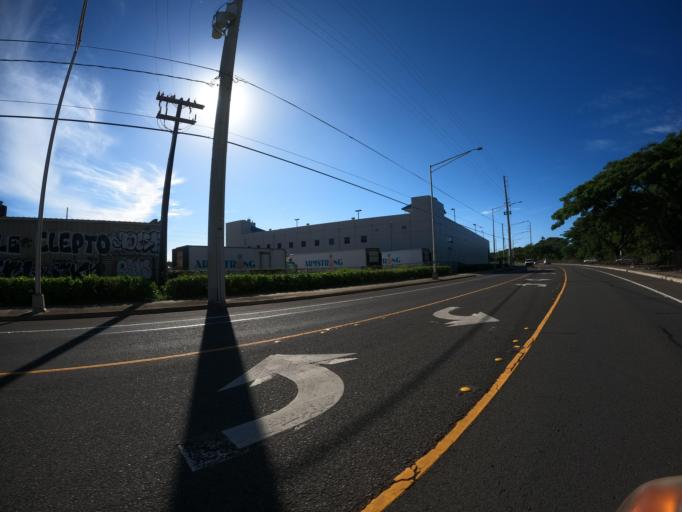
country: US
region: Hawaii
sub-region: Honolulu County
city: Halawa Heights
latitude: 21.3418
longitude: -157.9010
